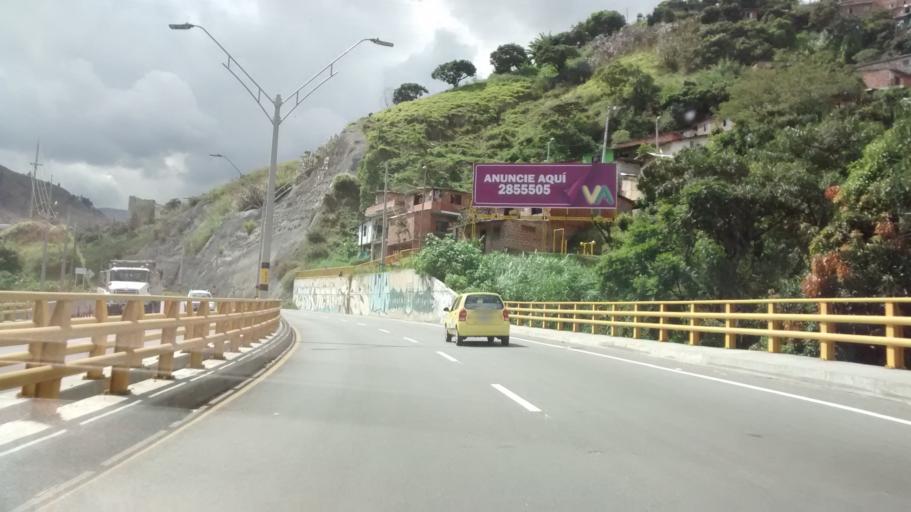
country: CO
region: Antioquia
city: Medellin
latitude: 6.2774
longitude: -75.6079
